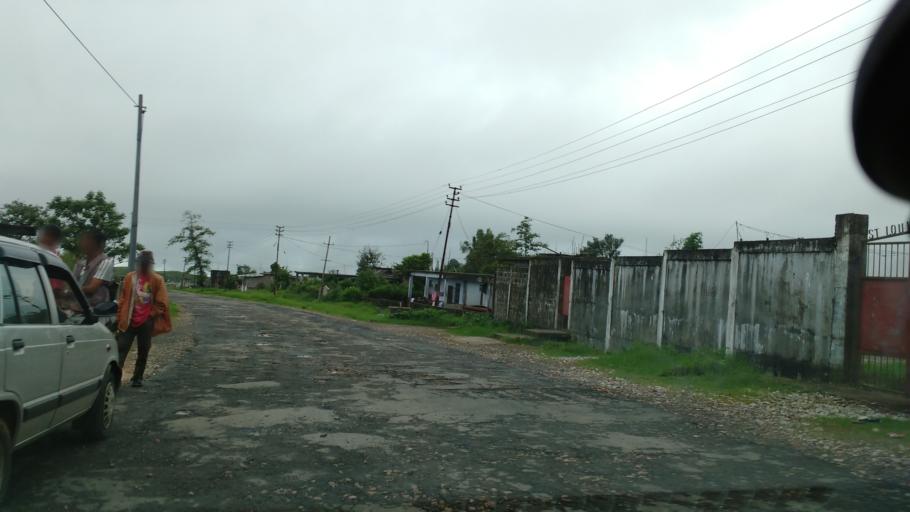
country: IN
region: Meghalaya
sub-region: East Khasi Hills
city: Cherrapunji
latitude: 25.2654
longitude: 91.7333
